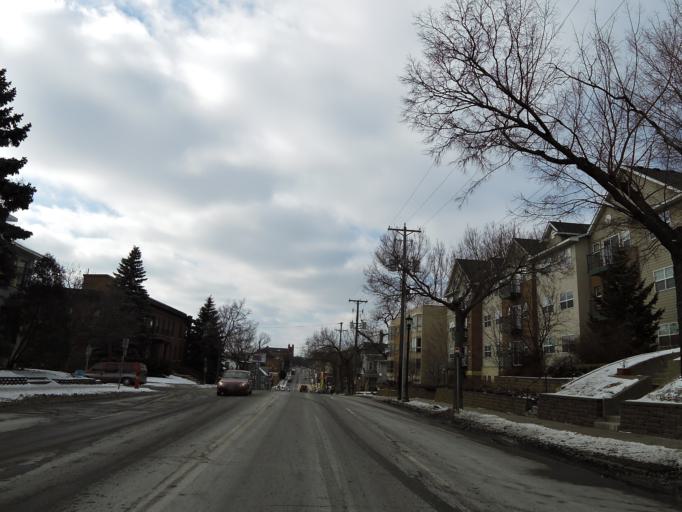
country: US
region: Minnesota
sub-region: Hennepin County
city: Minneapolis
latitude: 44.9627
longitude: -93.2849
